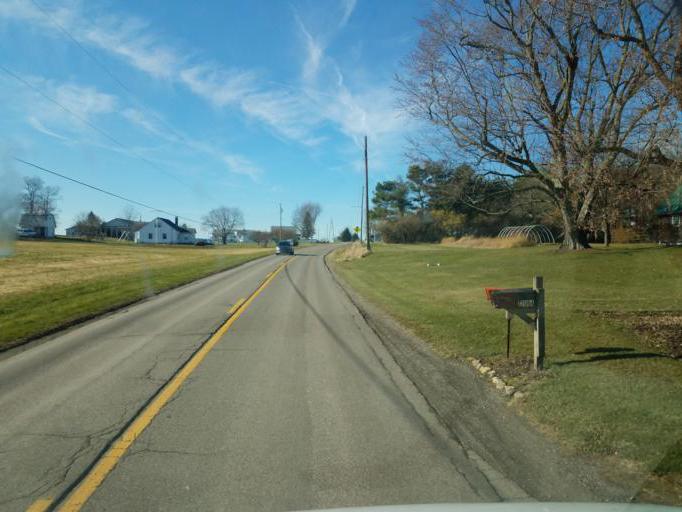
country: US
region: Ohio
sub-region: Wayne County
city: Apple Creek
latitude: 40.7412
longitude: -81.7640
